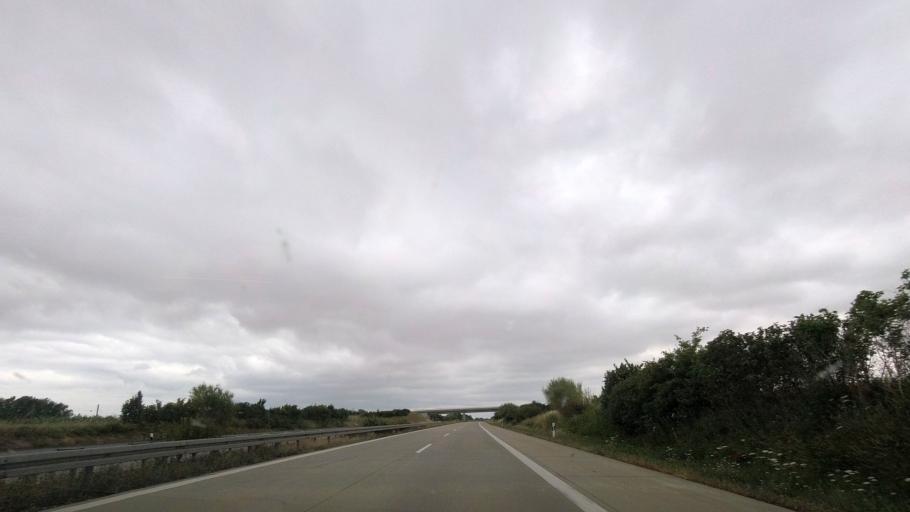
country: DE
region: Mecklenburg-Vorpommern
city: Gross Miltzow
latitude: 53.5508
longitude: 13.6020
